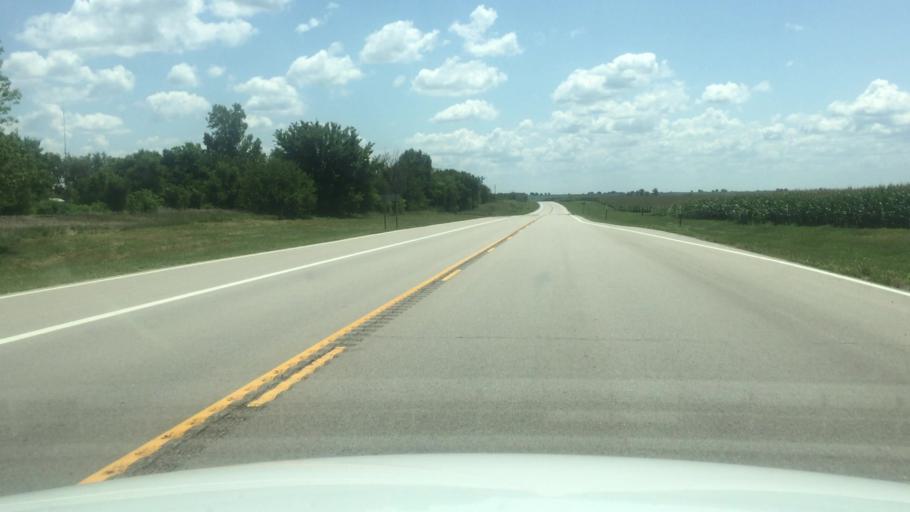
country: US
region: Kansas
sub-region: Brown County
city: Horton
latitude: 39.6379
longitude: -95.3536
